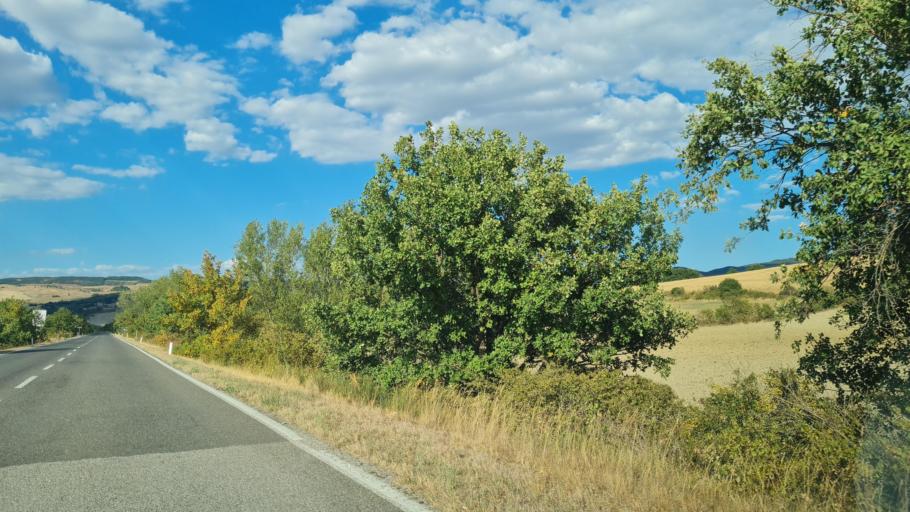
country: IT
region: Tuscany
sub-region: Provincia di Siena
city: Pienza
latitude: 42.9991
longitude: 11.7264
